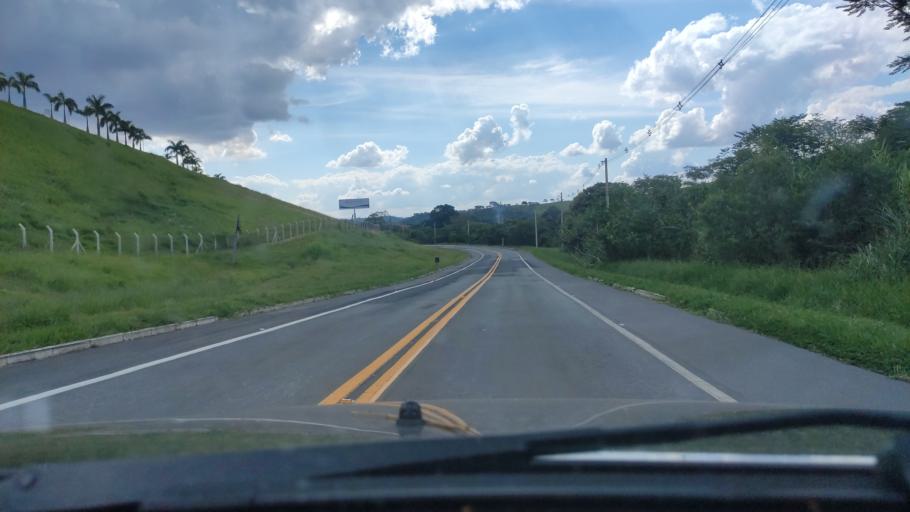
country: BR
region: Sao Paulo
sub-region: Aguas De Lindoia
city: Aguas de Lindoia
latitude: -22.4692
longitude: -46.7157
